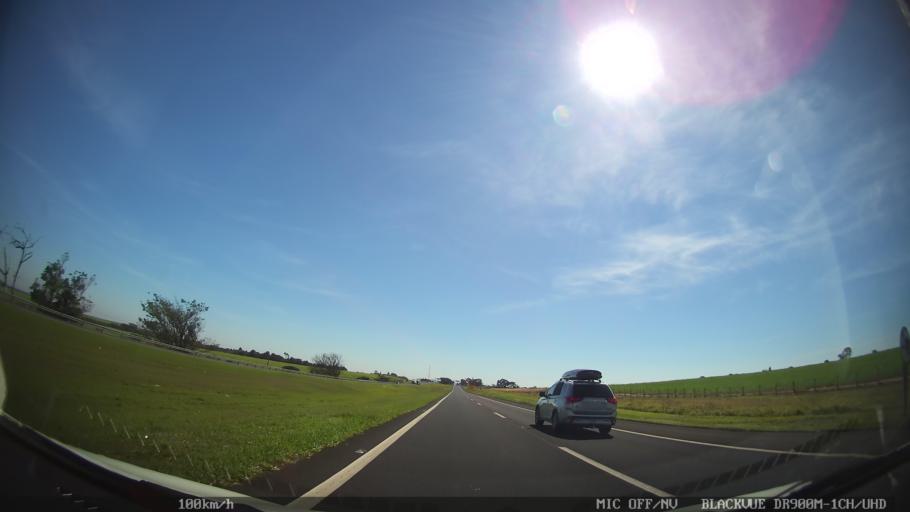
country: BR
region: Sao Paulo
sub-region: Santa Rita Do Passa Quatro
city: Santa Rita do Passa Quatro
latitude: -21.6913
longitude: -47.5992
